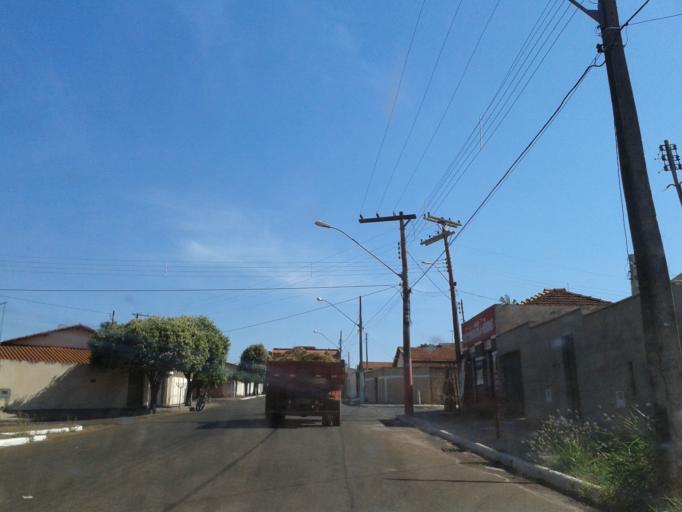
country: BR
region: Minas Gerais
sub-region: Ituiutaba
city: Ituiutaba
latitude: -18.9806
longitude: -49.4773
